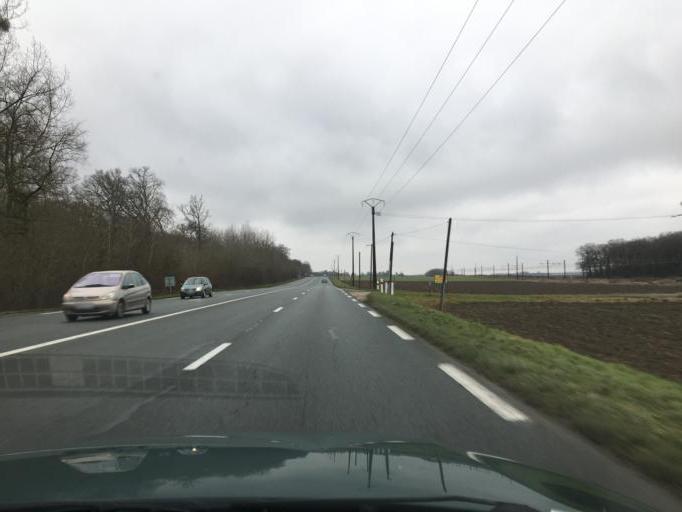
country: FR
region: Centre
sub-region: Departement du Loiret
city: Chevilly
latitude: 48.0117
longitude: 1.8785
